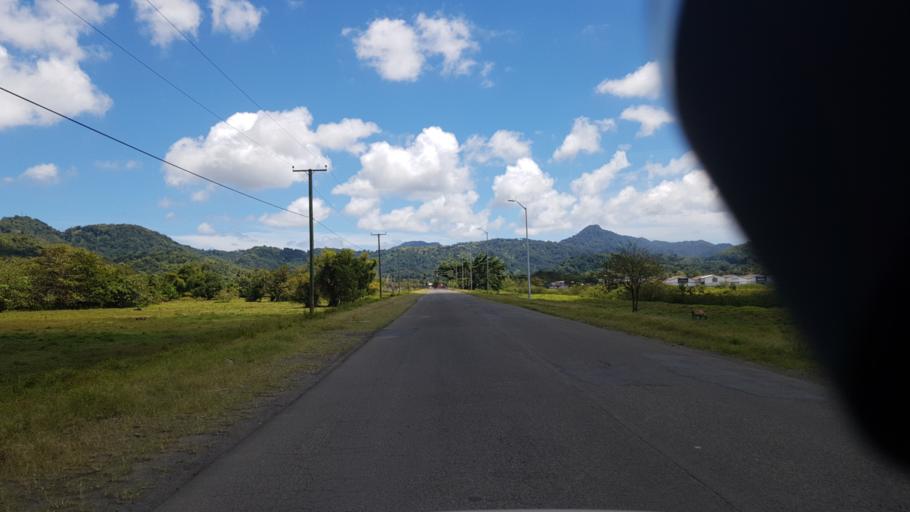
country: LC
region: Castries Quarter
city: Castries
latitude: 13.9833
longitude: -61.0029
